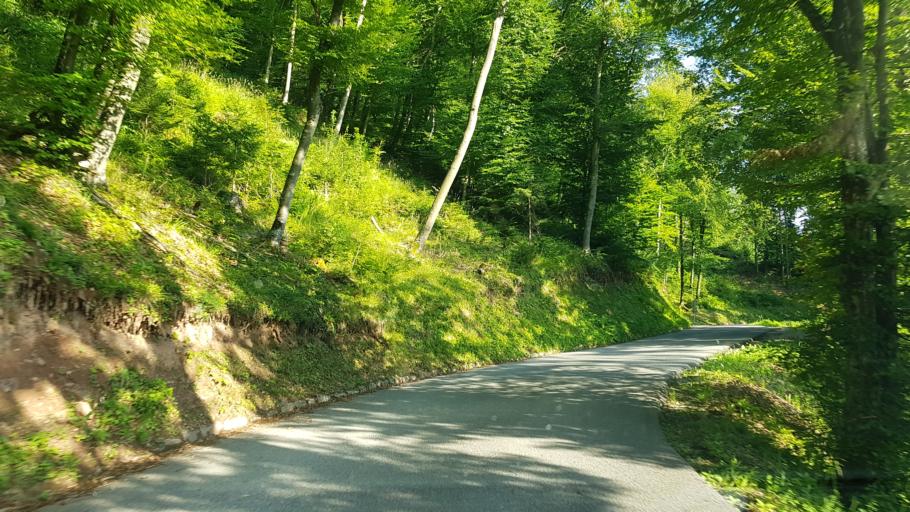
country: SI
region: Cerkno
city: Cerkno
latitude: 46.0787
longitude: 13.9993
